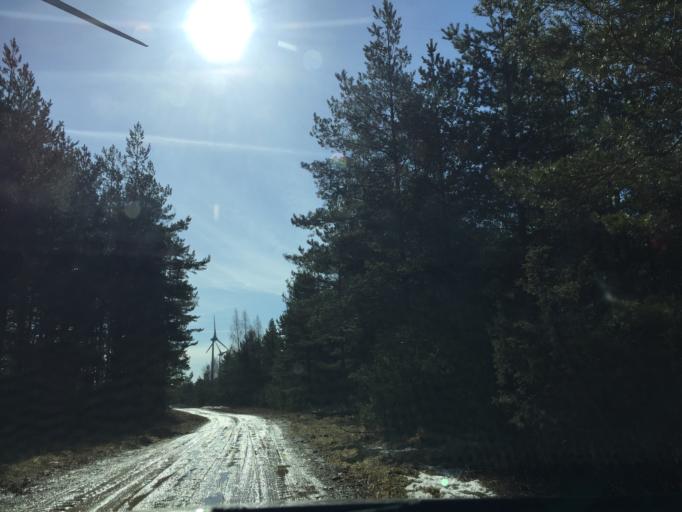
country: EE
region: Laeaene
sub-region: Haapsalu linn
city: Haapsalu
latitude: 58.6375
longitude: 23.5200
